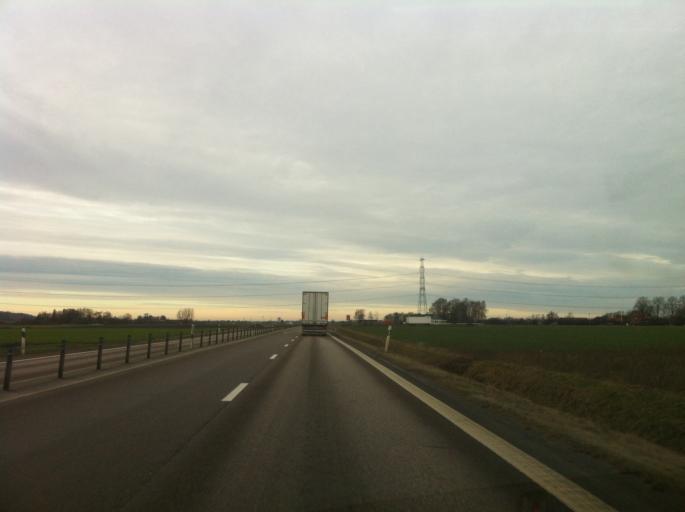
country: SE
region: Skane
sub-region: Astorps Kommun
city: Kvidinge
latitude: 56.1306
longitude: 13.0441
